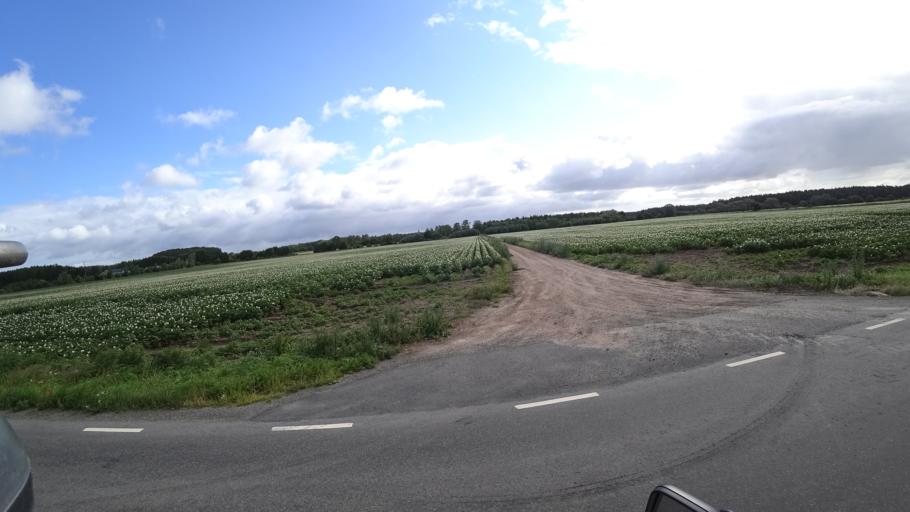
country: SE
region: Skane
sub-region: Kristianstads Kommun
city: Norra Asum
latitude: 55.9693
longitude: 14.1129
